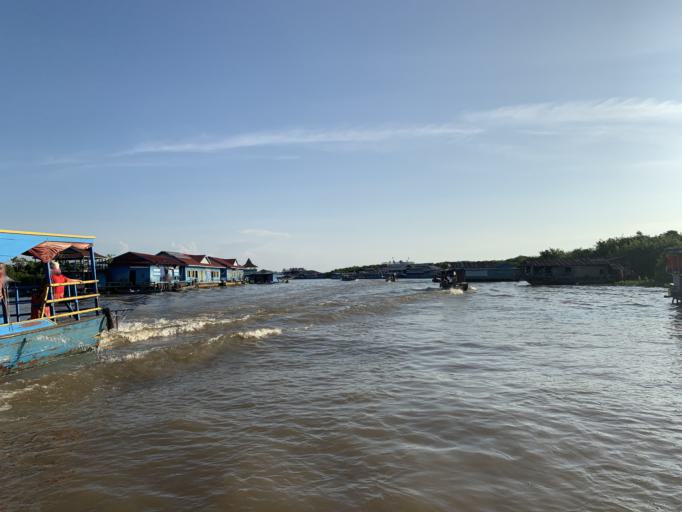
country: KH
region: Siem Reap
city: Siem Reap
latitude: 13.2453
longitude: 103.8230
